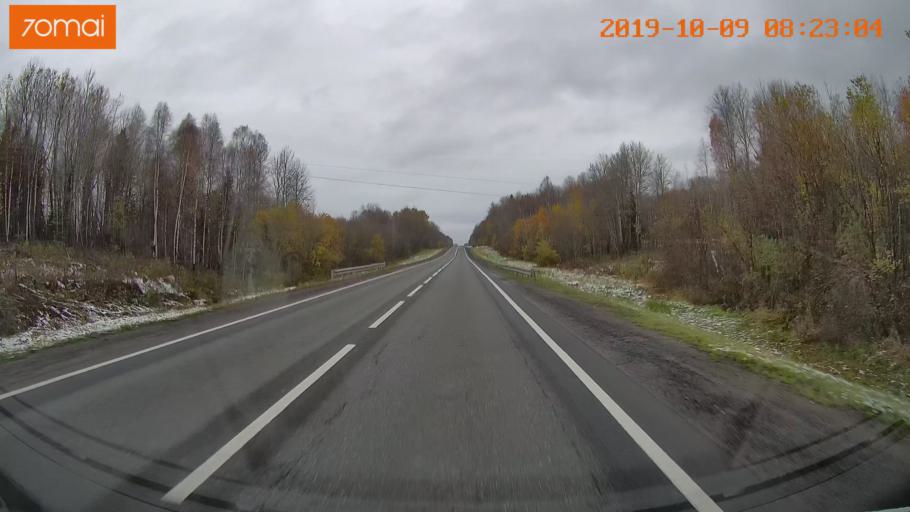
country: RU
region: Vologda
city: Gryazovets
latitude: 58.7497
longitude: 40.2853
